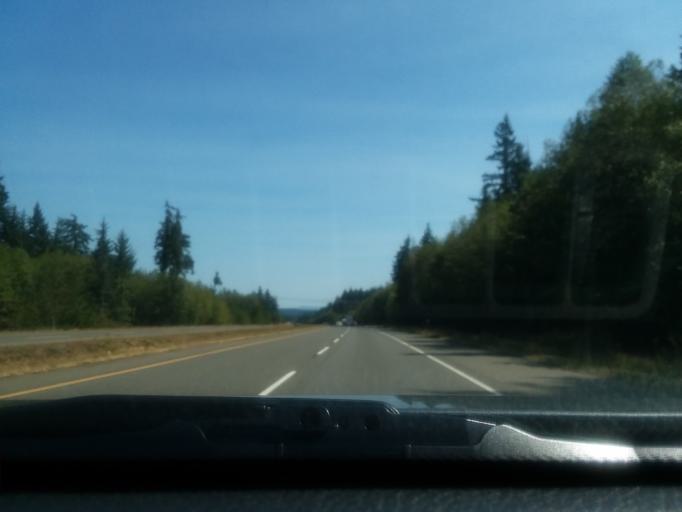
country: CA
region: British Columbia
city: Port Alberni
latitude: 49.4032
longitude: -124.6761
